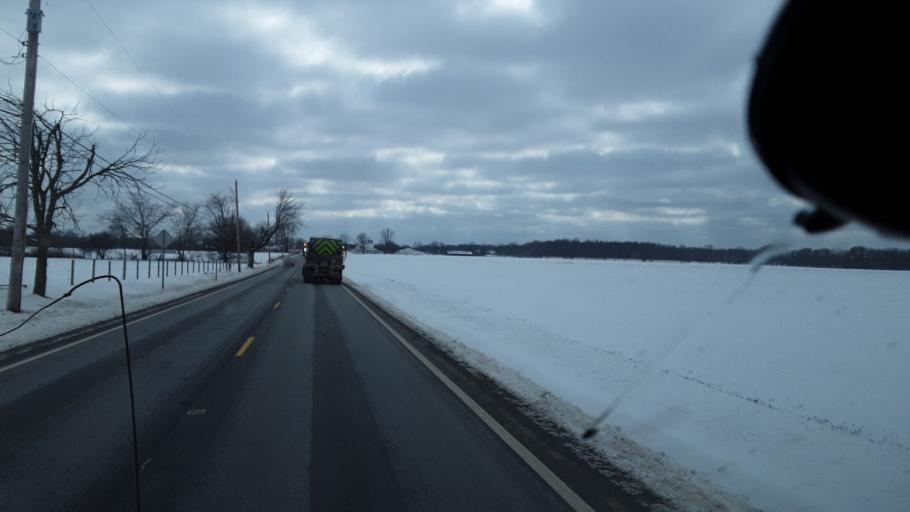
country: US
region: Ohio
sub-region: Delaware County
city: Sunbury
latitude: 40.2013
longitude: -82.8048
